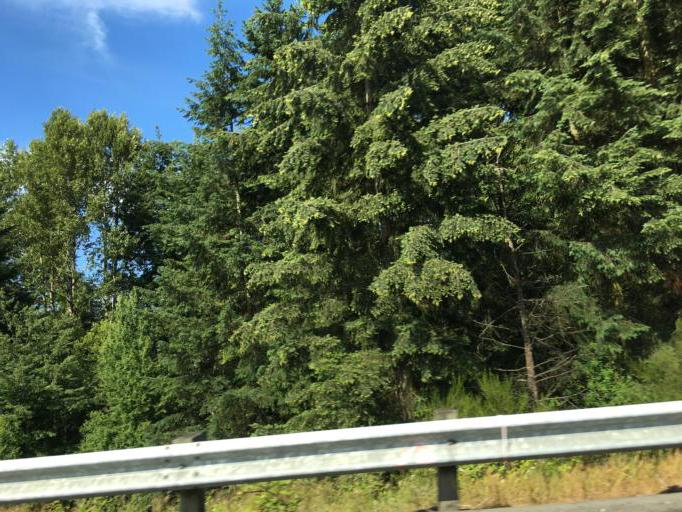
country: US
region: Washington
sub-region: Snohomish County
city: Mountlake Terrace
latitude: 47.7789
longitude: -122.3163
